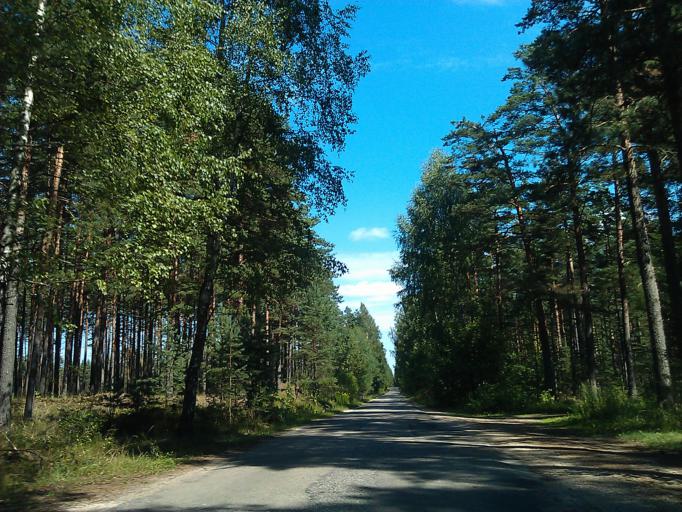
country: LV
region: Riga
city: Bergi
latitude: 57.0045
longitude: 24.3133
